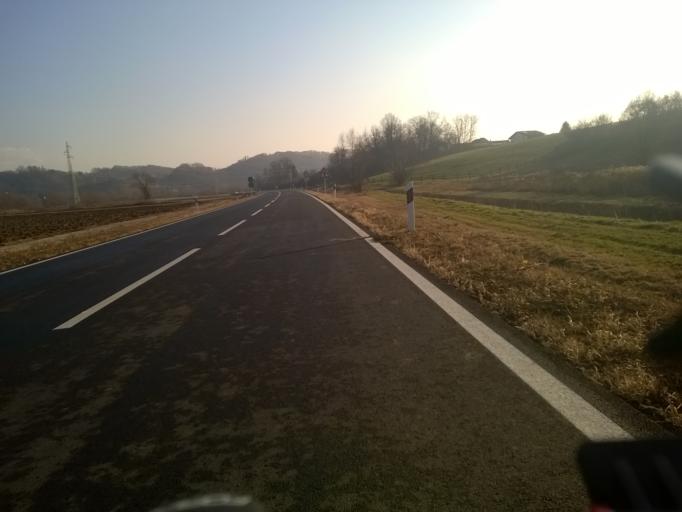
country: HR
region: Krapinsko-Zagorska
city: Zabok
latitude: 46.0397
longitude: 15.9169
